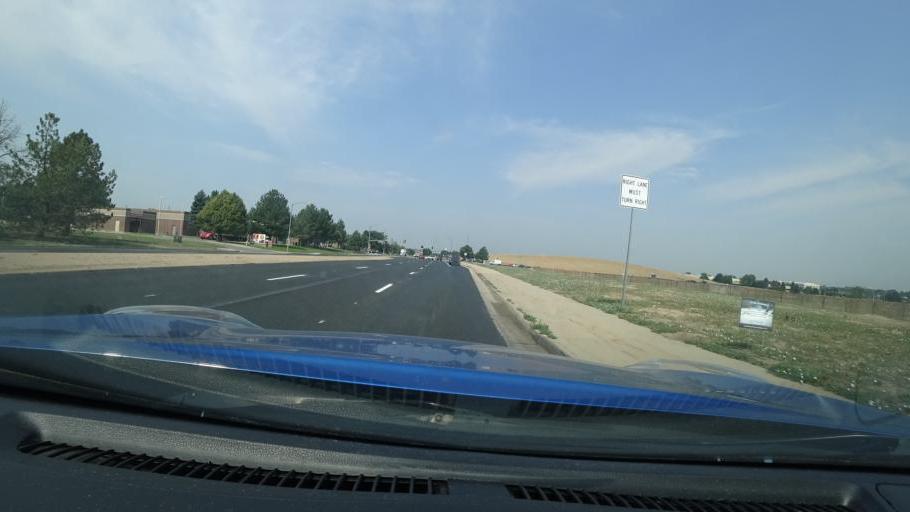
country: US
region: Colorado
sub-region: Adams County
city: Aurora
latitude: 39.7065
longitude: -104.7888
